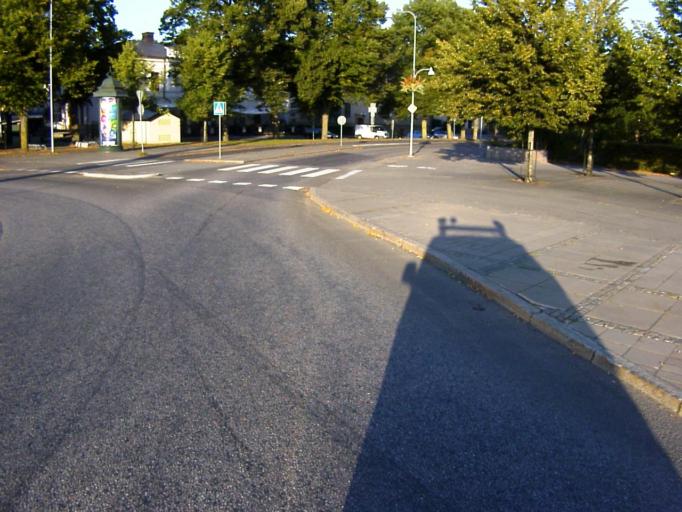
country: SE
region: Soedermanland
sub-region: Eskilstuna Kommun
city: Eskilstuna
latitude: 59.3730
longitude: 16.5158
